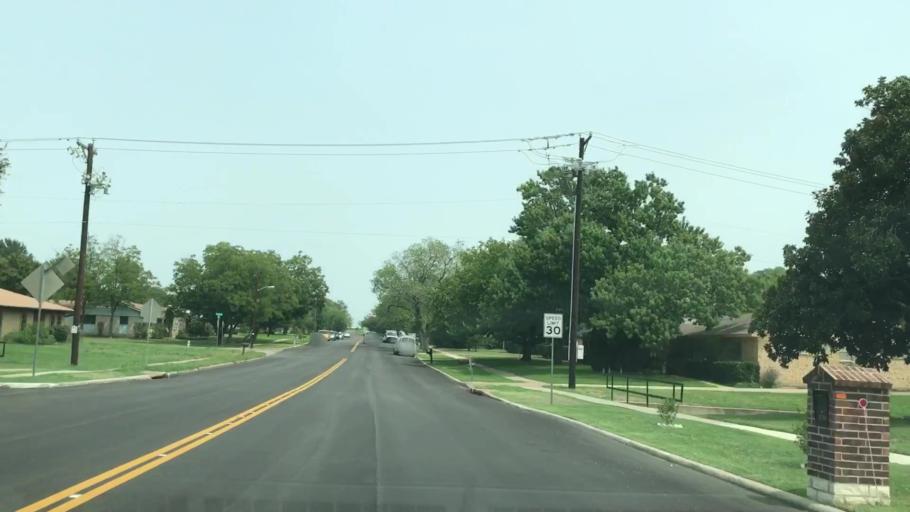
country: US
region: Texas
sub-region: Dallas County
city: Irving
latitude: 32.8475
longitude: -97.0004
